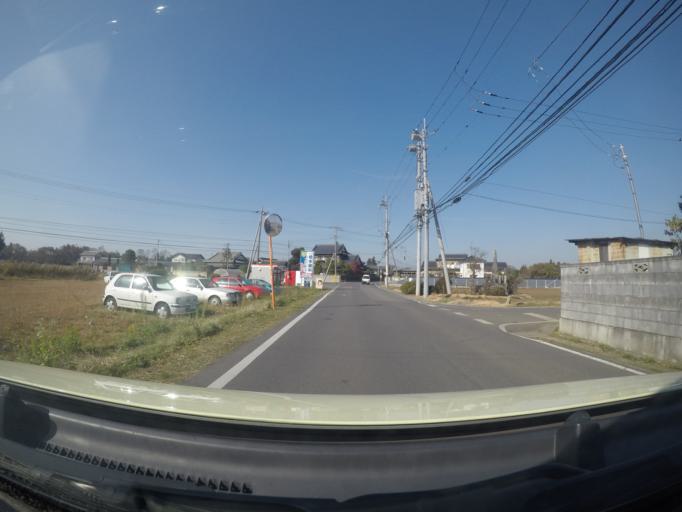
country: JP
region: Ibaraki
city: Tsukuba
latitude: 36.1295
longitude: 140.0986
